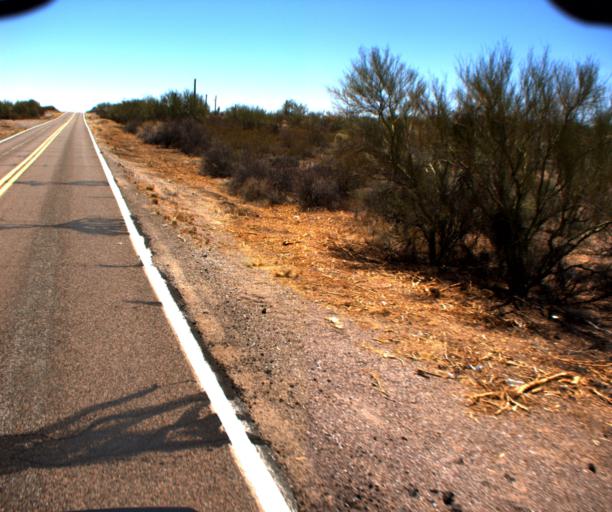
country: US
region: Arizona
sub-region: Pima County
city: Ajo
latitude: 32.2097
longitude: -112.6203
